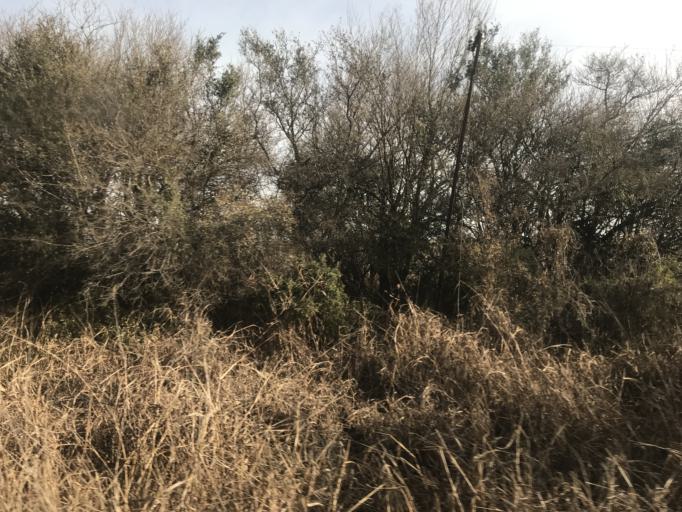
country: AR
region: Cordoba
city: Laguna Larga
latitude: -31.7627
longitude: -63.8152
